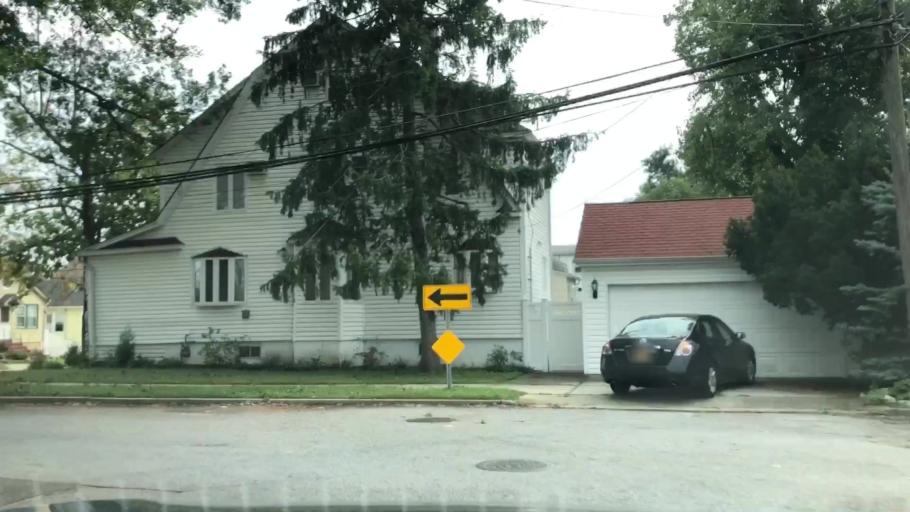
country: US
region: New York
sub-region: Nassau County
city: South Floral Park
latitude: 40.7068
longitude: -73.6914
